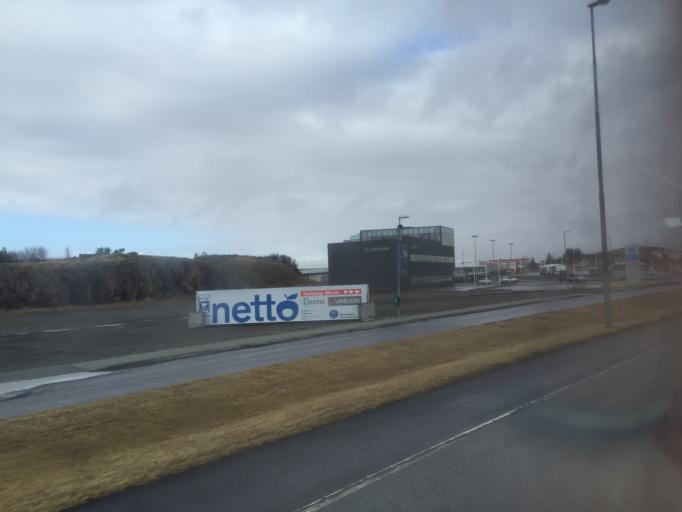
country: IS
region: West
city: Borgarnes
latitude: 64.5420
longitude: -21.9081
